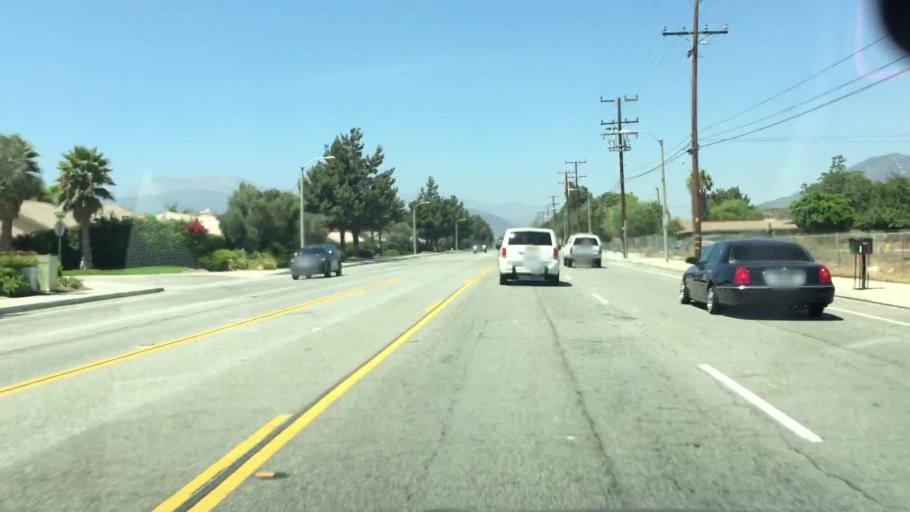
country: US
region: California
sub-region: San Bernardino County
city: Muscoy
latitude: 34.1837
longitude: -117.3458
